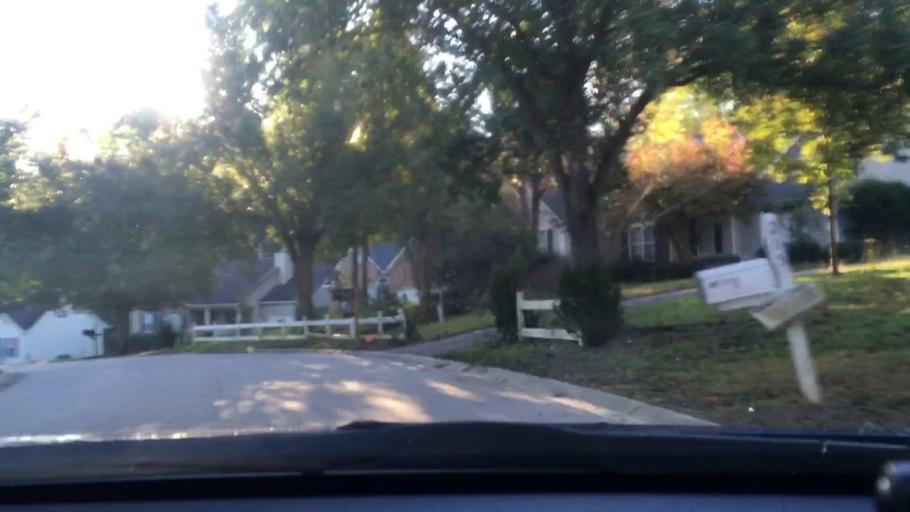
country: US
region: South Carolina
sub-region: Lexington County
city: Irmo
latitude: 34.1161
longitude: -81.1734
